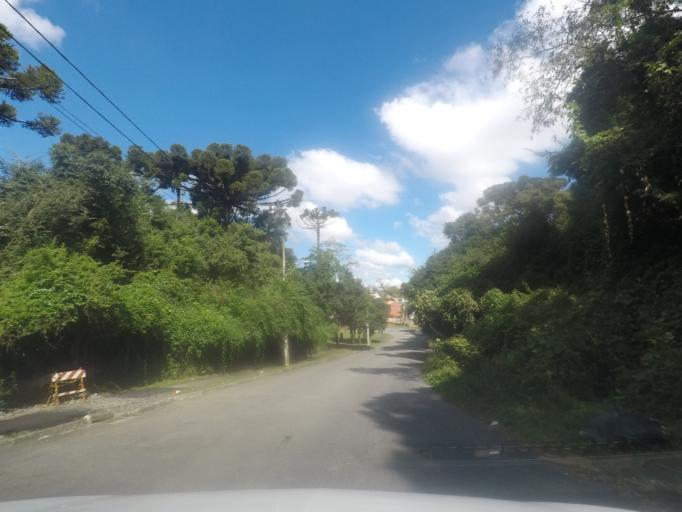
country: BR
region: Parana
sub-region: Pinhais
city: Pinhais
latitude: -25.4771
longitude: -49.2211
